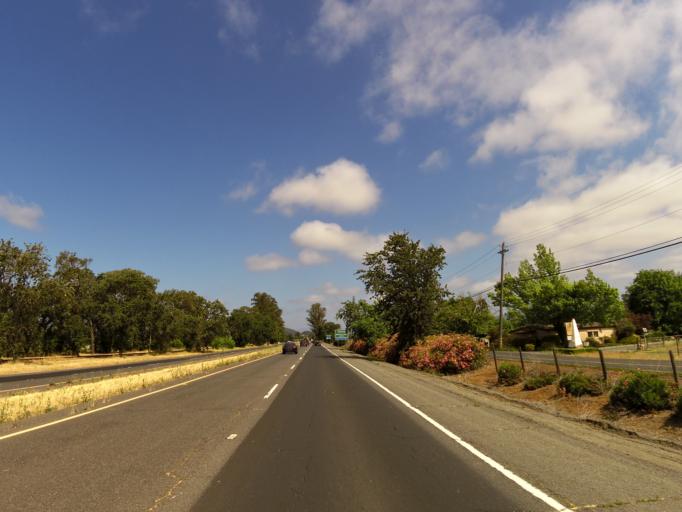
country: US
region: California
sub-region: Napa County
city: Yountville
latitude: 38.3867
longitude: -122.3499
